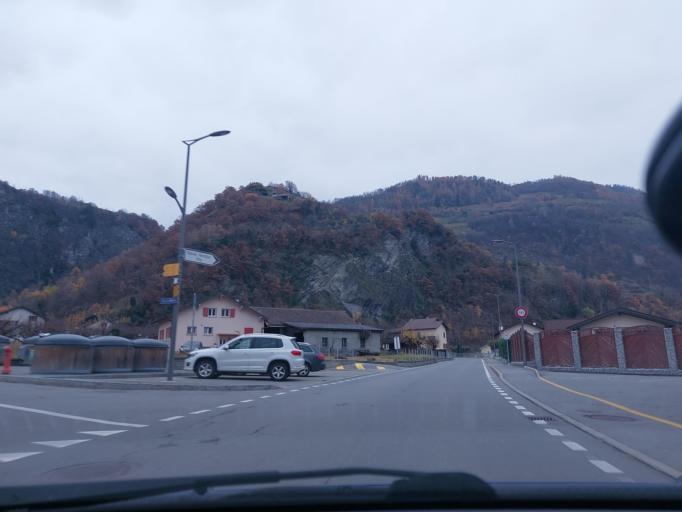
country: CH
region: Valais
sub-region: Conthey District
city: Basse-Nendaz
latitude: 46.2064
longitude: 7.3161
